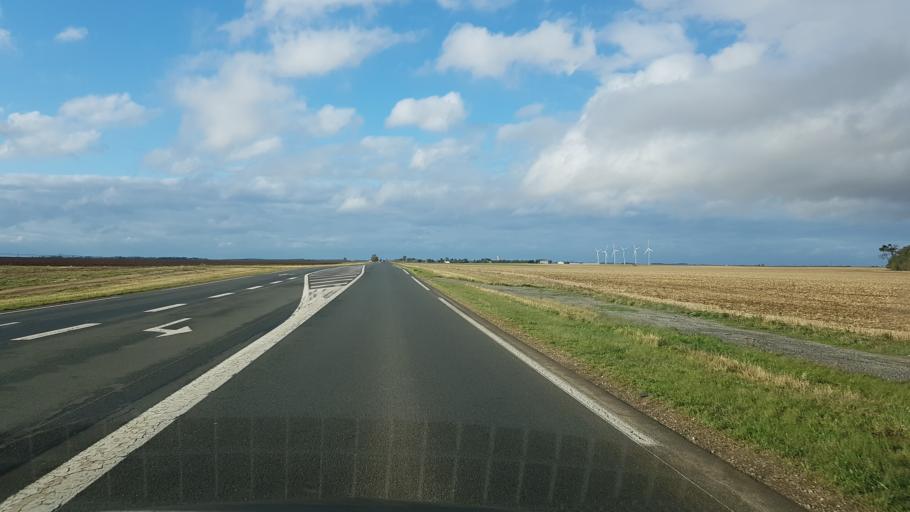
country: FR
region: Centre
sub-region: Departement du Loiret
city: Sermaises
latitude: 48.2420
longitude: 2.2207
